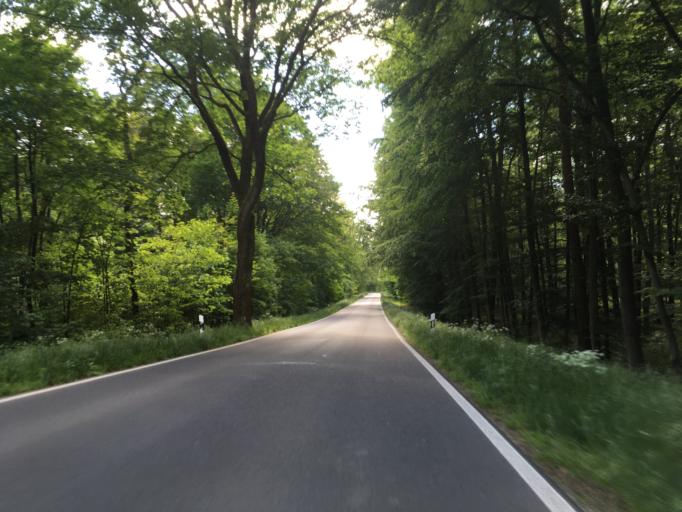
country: DE
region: Brandenburg
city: Protzel
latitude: 52.5996
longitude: 13.9829
